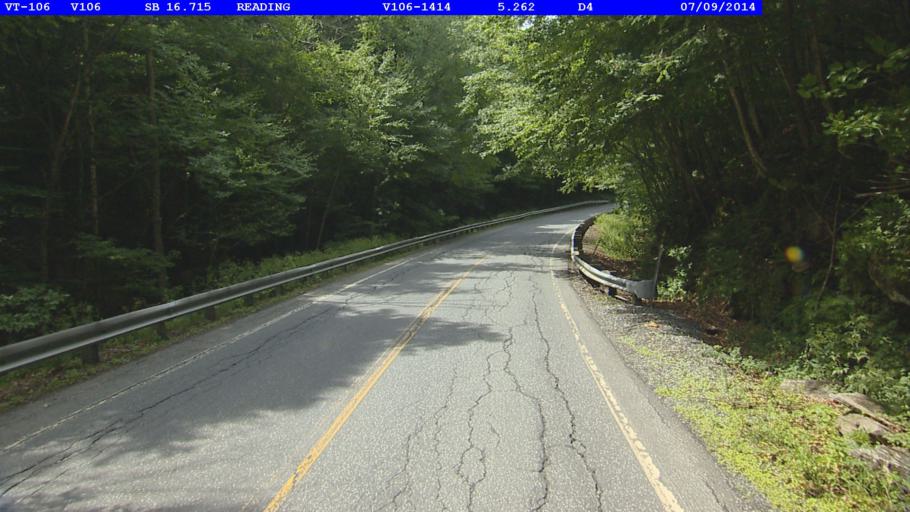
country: US
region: Vermont
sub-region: Windsor County
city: Woodstock
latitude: 43.5111
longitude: -72.5497
